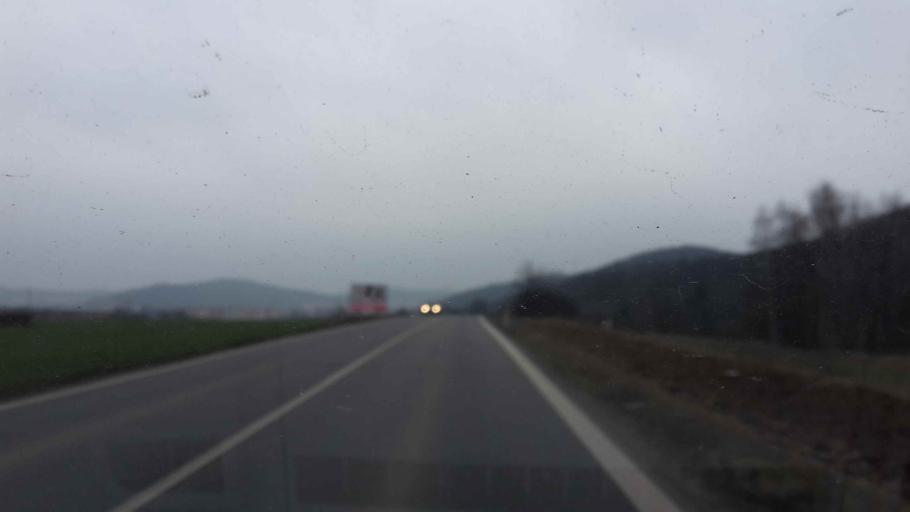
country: CZ
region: South Moravian
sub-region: Okres Brno-Venkov
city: Lelekovice
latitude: 49.2937
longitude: 16.5552
